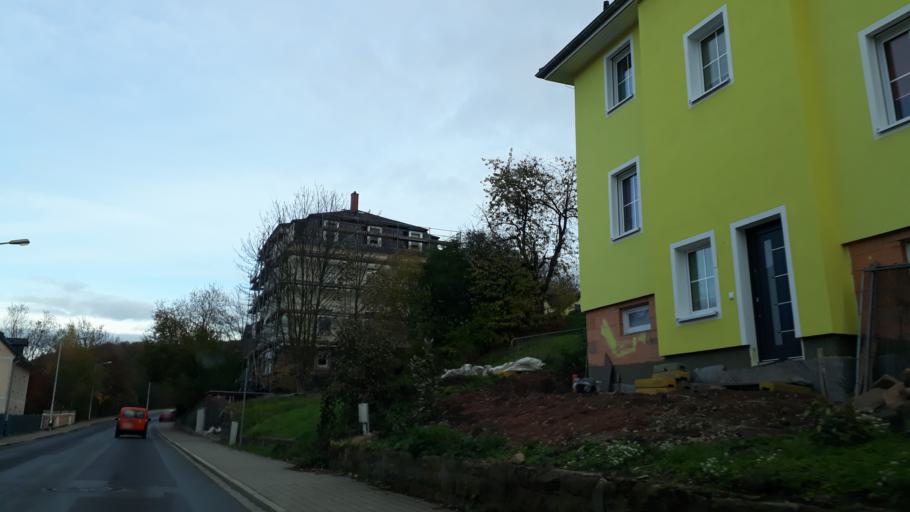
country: DE
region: Saxony
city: Rabenau
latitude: 50.9786
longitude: 13.6265
